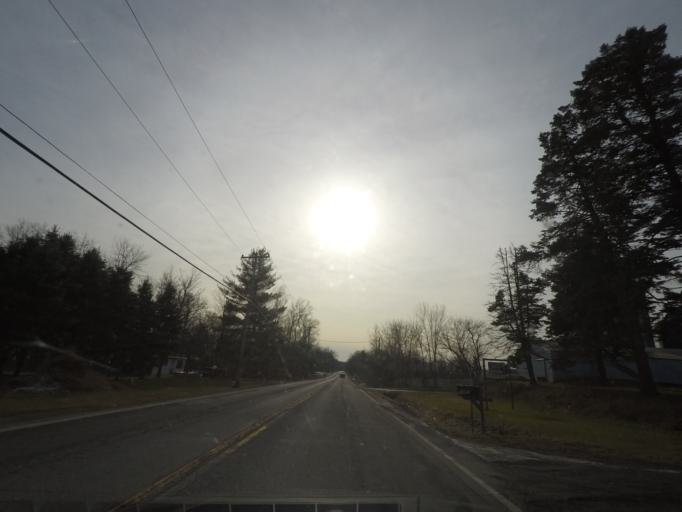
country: US
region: New York
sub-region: Saratoga County
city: Stillwater
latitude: 42.9689
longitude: -73.6335
